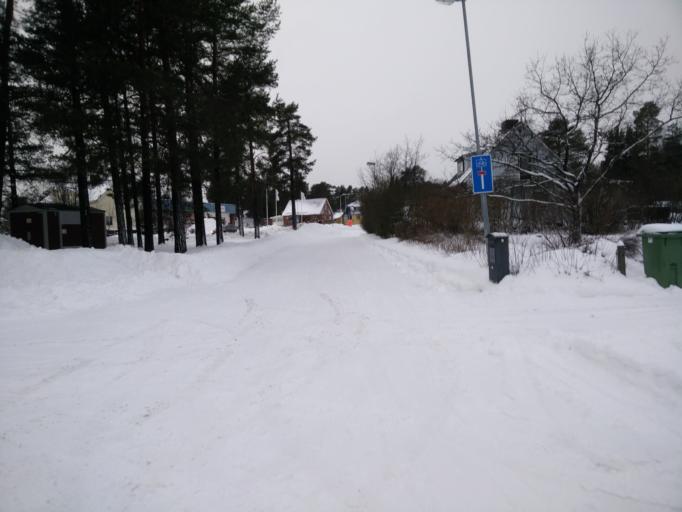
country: SE
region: Vaesternorrland
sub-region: Sundsvalls Kommun
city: Nolby
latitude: 62.2908
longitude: 17.3709
